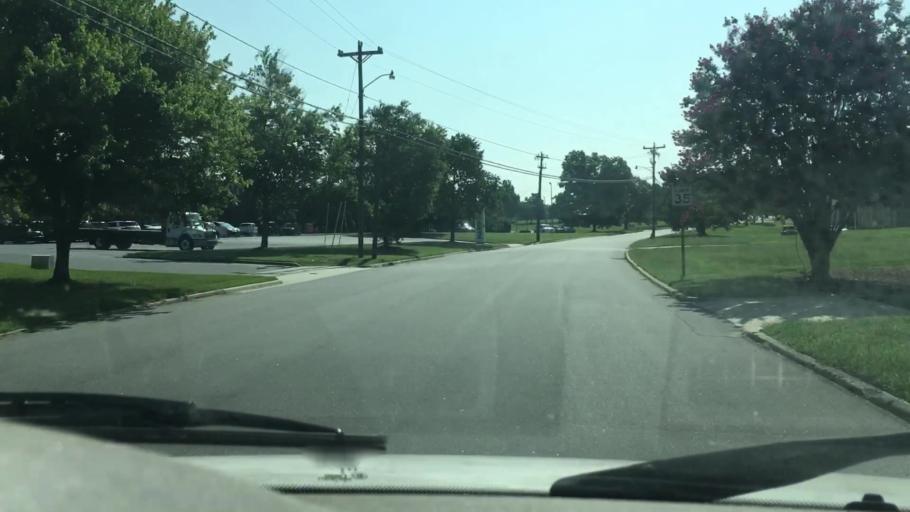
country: US
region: North Carolina
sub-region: Mecklenburg County
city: Charlotte
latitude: 35.2242
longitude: -80.9158
